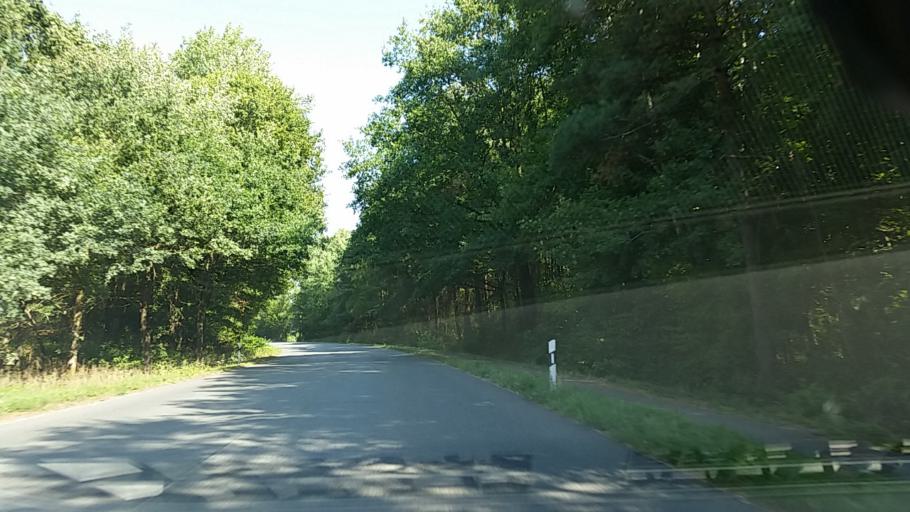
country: DE
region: Lower Saxony
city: Uelzen
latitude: 52.9906
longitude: 10.5686
